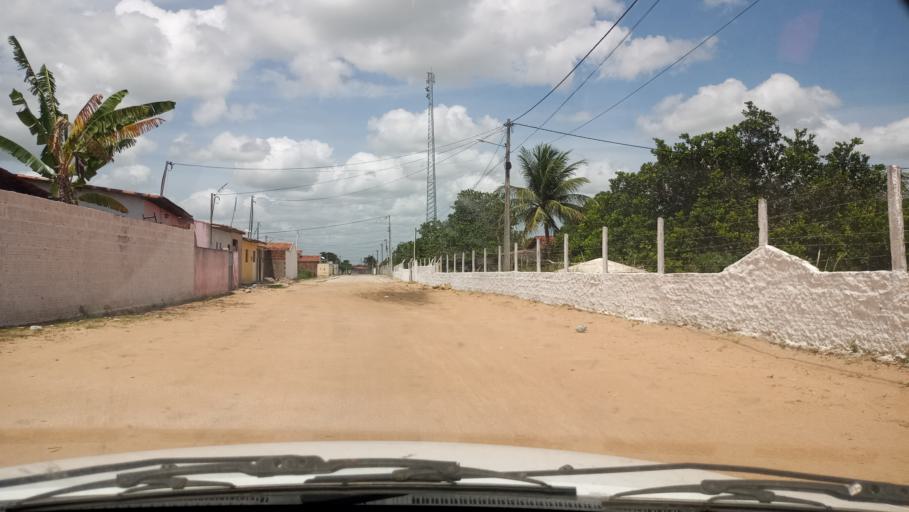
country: BR
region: Rio Grande do Norte
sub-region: Brejinho
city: Brejinho
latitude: -6.2650
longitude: -35.3720
